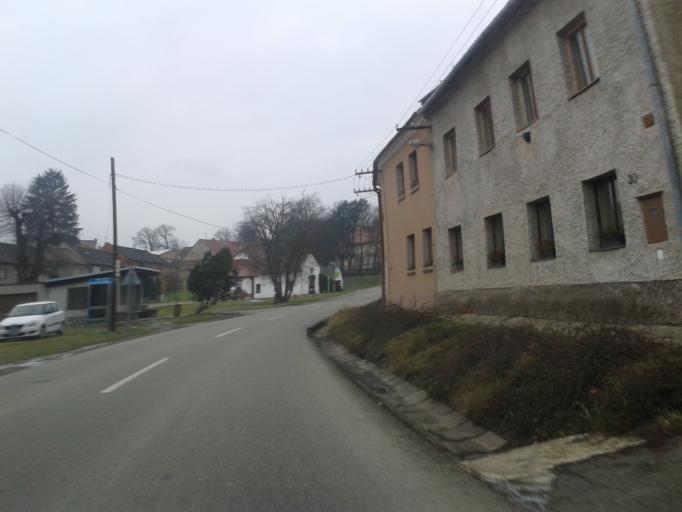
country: CZ
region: Olomoucky
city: Premyslovice
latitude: 49.5834
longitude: 17.0042
